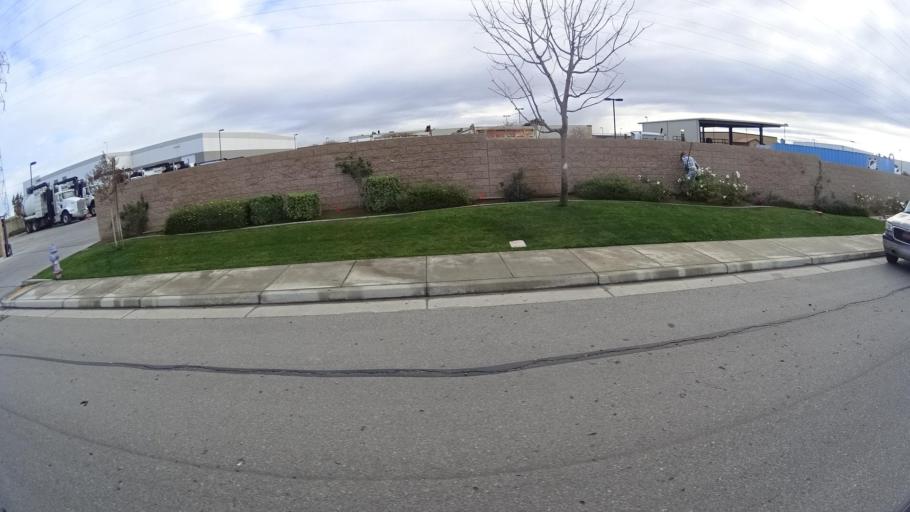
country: US
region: California
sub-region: Kern County
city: Oildale
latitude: 35.4548
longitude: -119.0826
